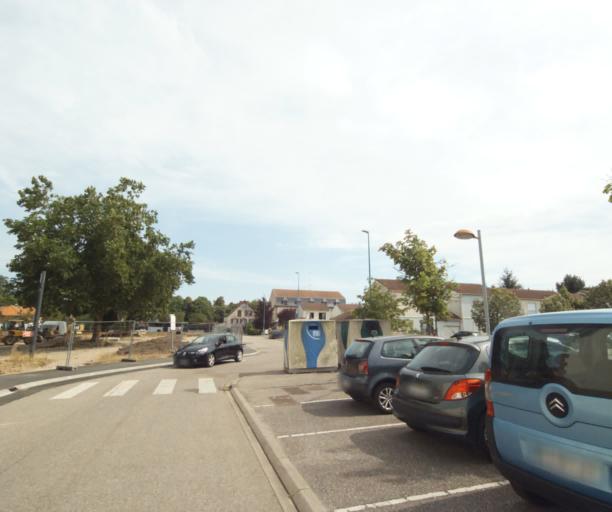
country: FR
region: Lorraine
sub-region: Departement de Meurthe-et-Moselle
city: Luneville
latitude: 48.5920
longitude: 6.5004
